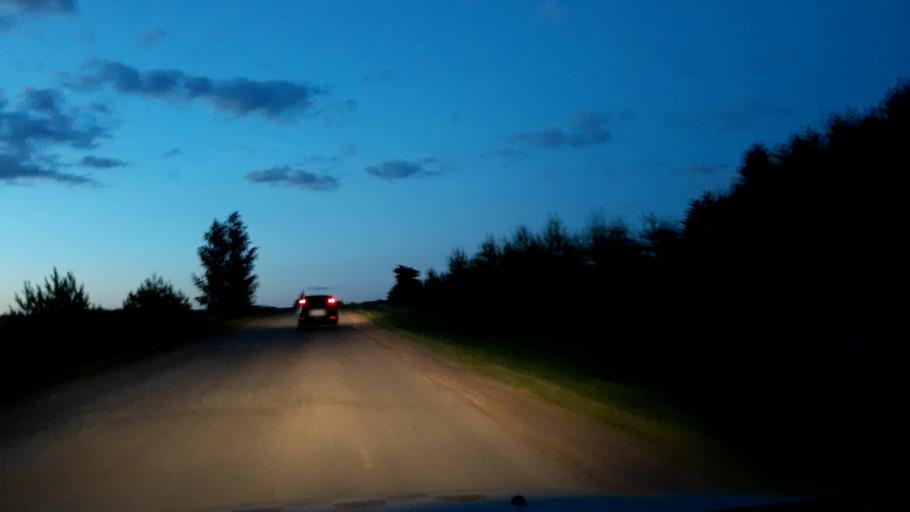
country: RU
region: Nizjnij Novgorod
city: Pamyat' Parizhskoy Kommuny
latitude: 56.0567
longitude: 44.4519
